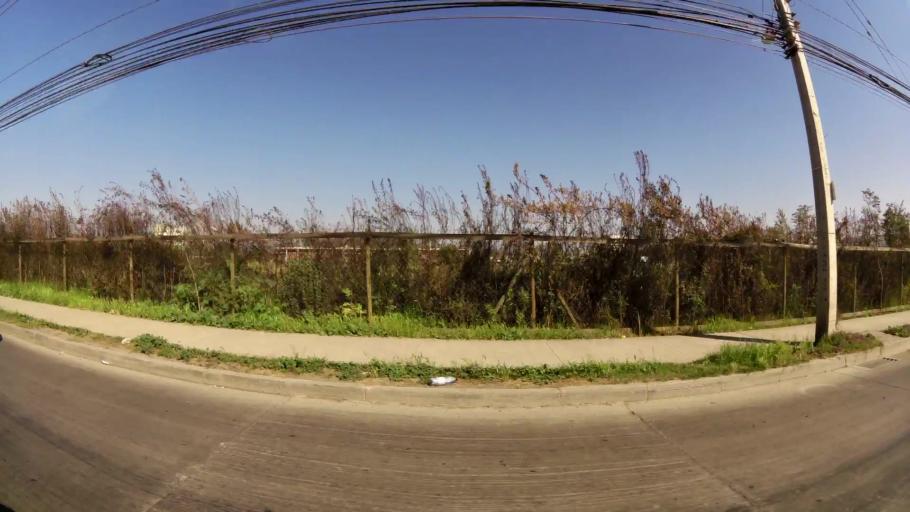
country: CL
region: Santiago Metropolitan
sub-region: Provincia de Chacabuco
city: Chicureo Abajo
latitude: -33.3687
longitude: -70.6711
